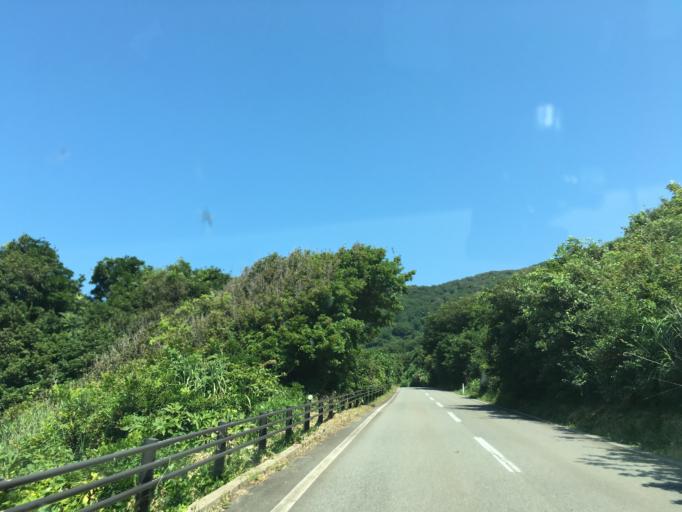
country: JP
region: Akita
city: Tenno
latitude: 39.9271
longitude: 139.7127
